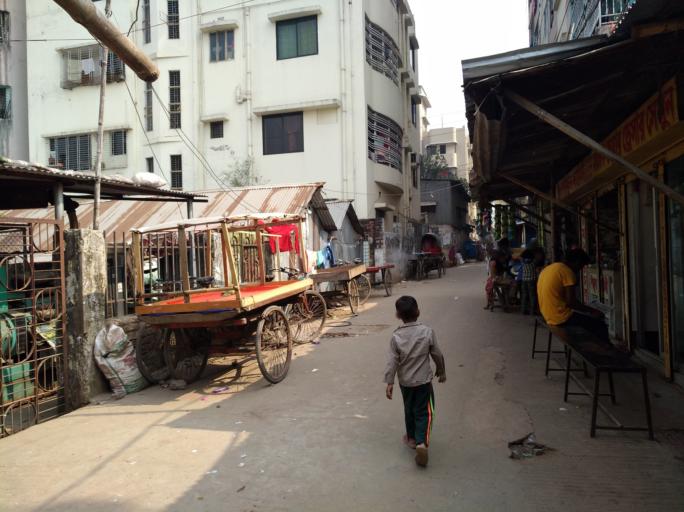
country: BD
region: Dhaka
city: Tungi
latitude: 23.8289
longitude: 90.3619
